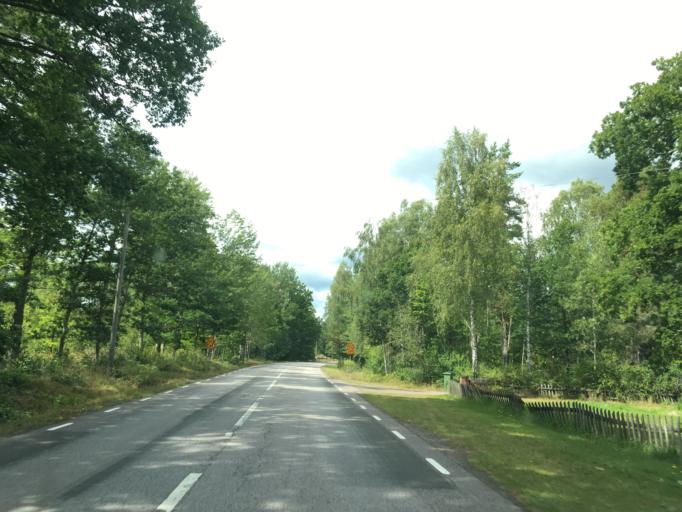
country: SE
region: Kalmar
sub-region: Nybro Kommun
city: Nybro
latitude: 56.9311
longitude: 15.9196
